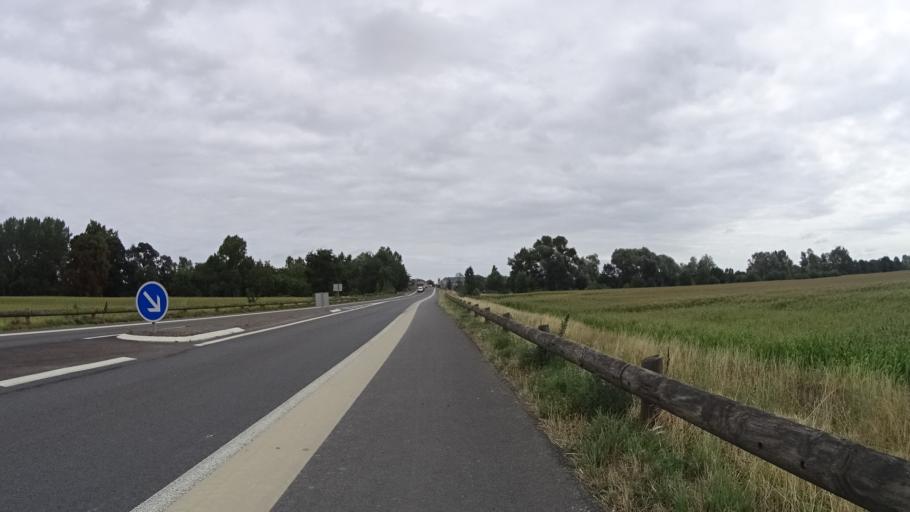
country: FR
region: Pays de la Loire
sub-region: Departement de Maine-et-Loire
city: Chalonnes-sur-Loire
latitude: 47.3652
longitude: -0.7558
